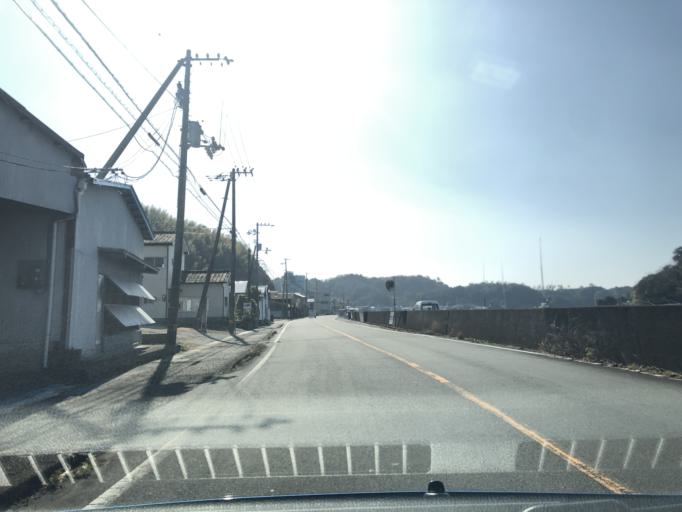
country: JP
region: Kochi
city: Sukumo
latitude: 32.9249
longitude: 132.6957
